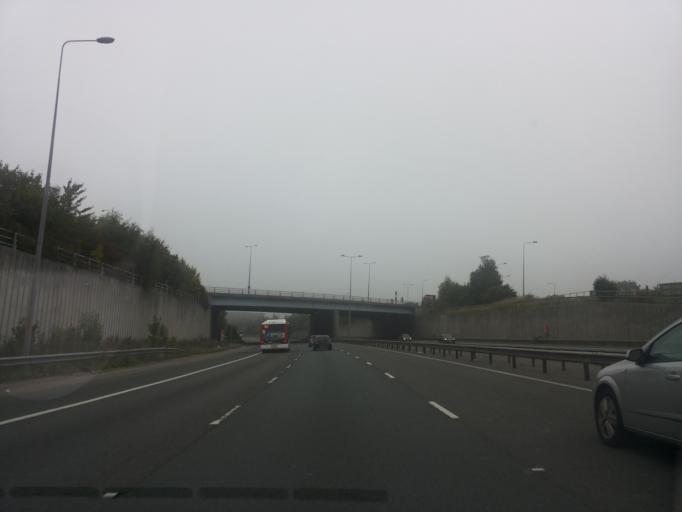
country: GB
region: England
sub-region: Borough of Tameside
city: Ashton-under-Lyne
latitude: 53.4808
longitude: -2.1168
